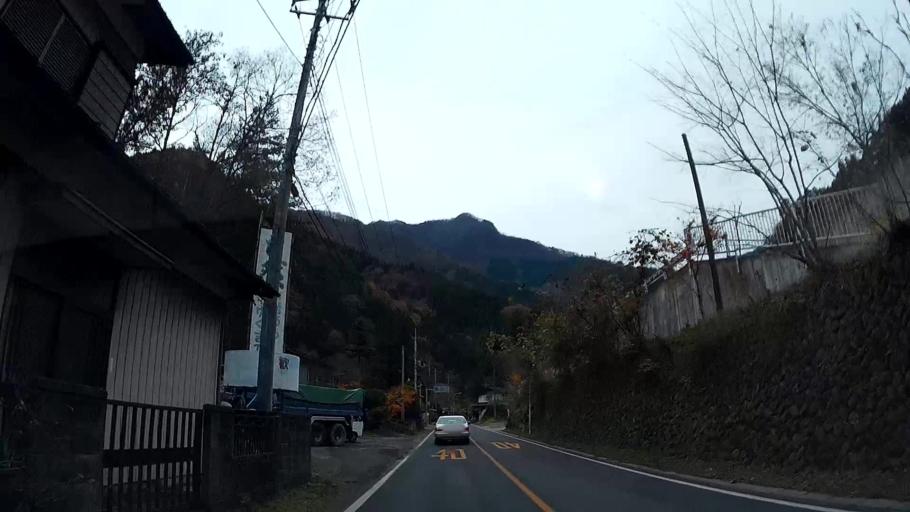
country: JP
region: Saitama
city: Chichibu
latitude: 35.9404
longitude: 138.9551
